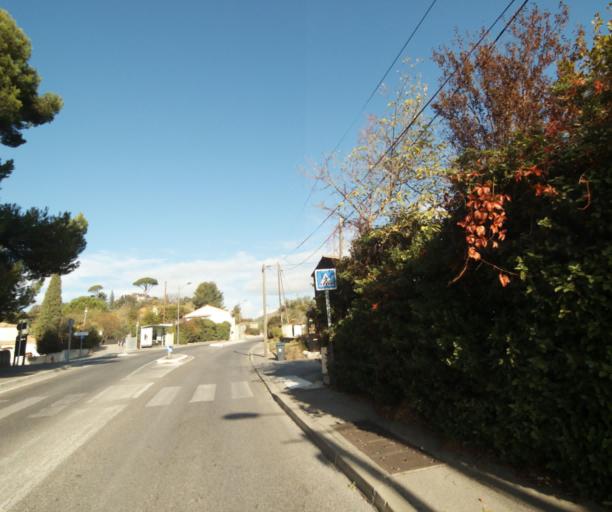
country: FR
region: Provence-Alpes-Cote d'Azur
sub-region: Departement des Bouches-du-Rhone
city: Allauch
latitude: 43.3233
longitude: 5.4923
